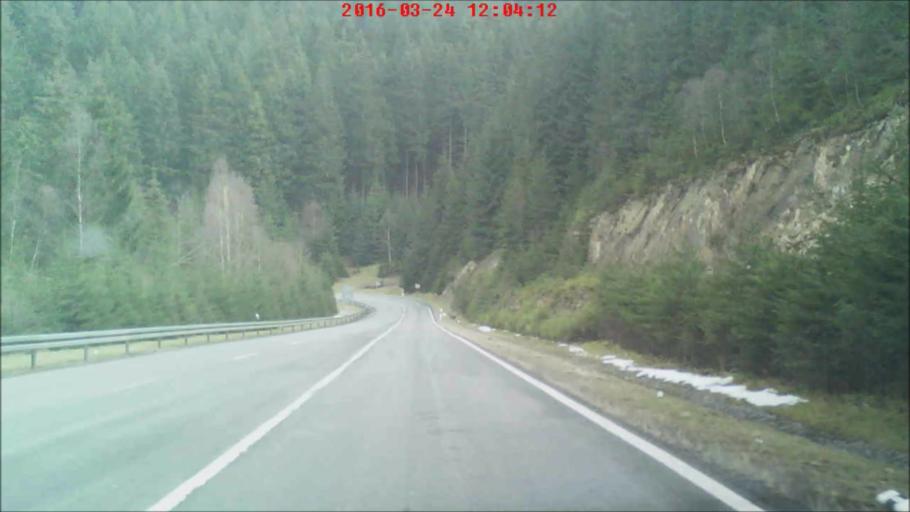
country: DE
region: Thuringia
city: Goldisthal
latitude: 50.5160
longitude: 11.0063
